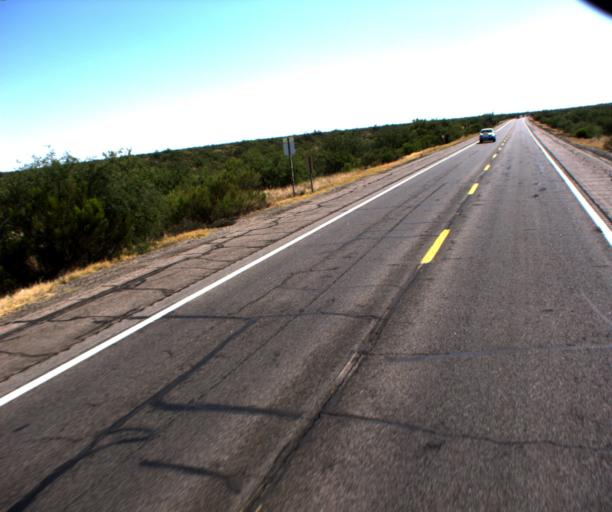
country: US
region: Arizona
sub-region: Pinal County
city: Oracle
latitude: 32.6070
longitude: -110.8557
